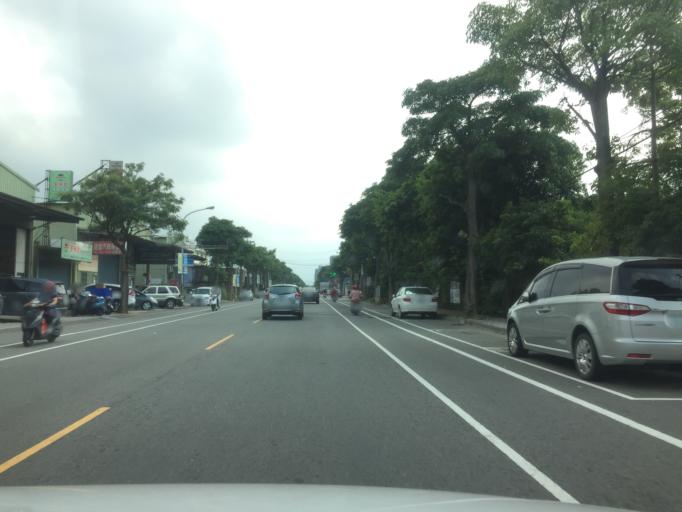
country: TW
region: Taiwan
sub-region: Taoyuan
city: Taoyuan
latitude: 24.9731
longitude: 121.3069
